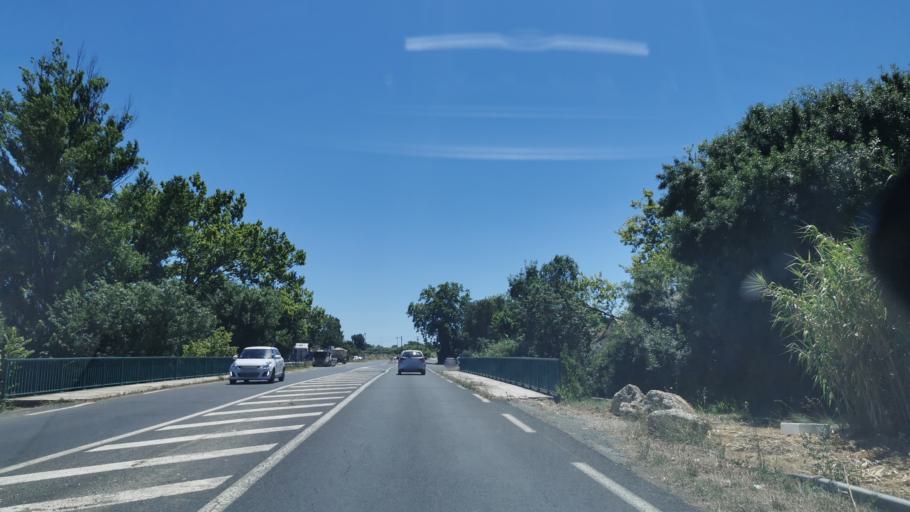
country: FR
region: Languedoc-Roussillon
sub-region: Departement de l'Herault
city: Beziers
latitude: 43.3309
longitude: 3.1940
